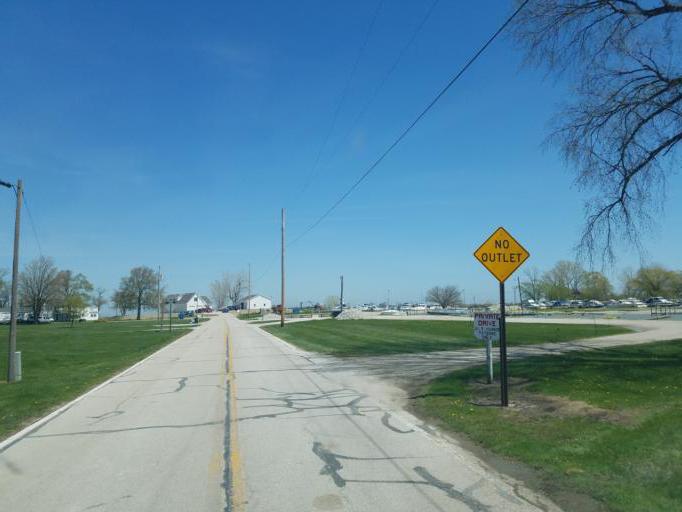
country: US
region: Ohio
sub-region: Ottawa County
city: Oak Harbor
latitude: 41.6108
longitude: -83.1064
